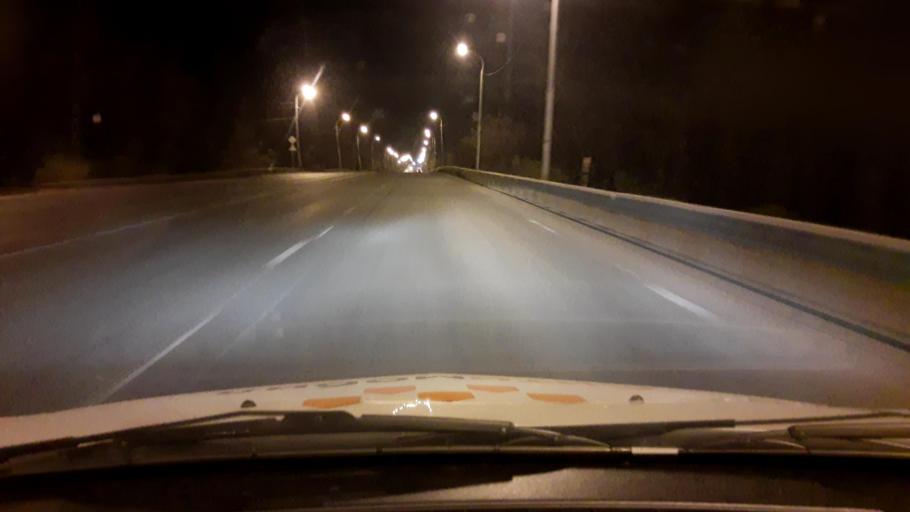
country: RU
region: Bashkortostan
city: Iglino
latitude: 54.7948
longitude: 56.2086
